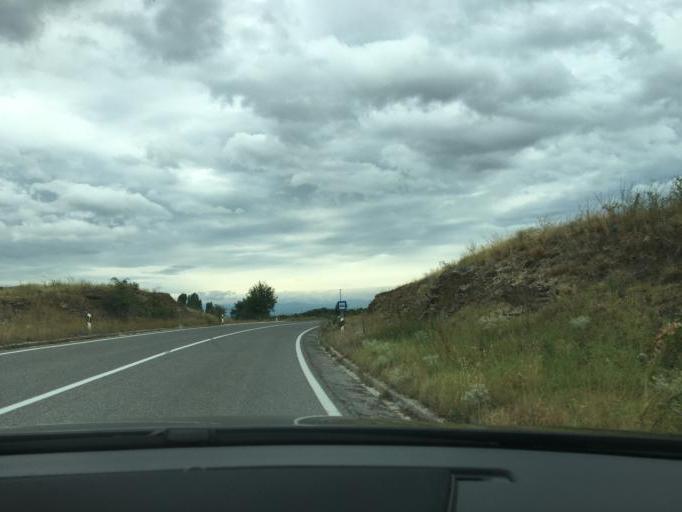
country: MK
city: Klechovce
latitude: 42.1474
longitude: 21.9783
